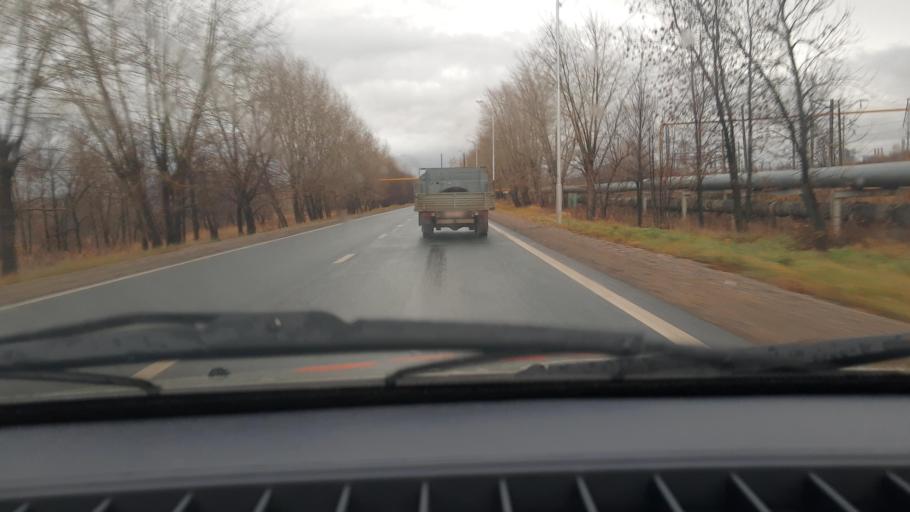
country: RU
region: Bashkortostan
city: Ufa
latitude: 54.8564
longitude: 56.1149
